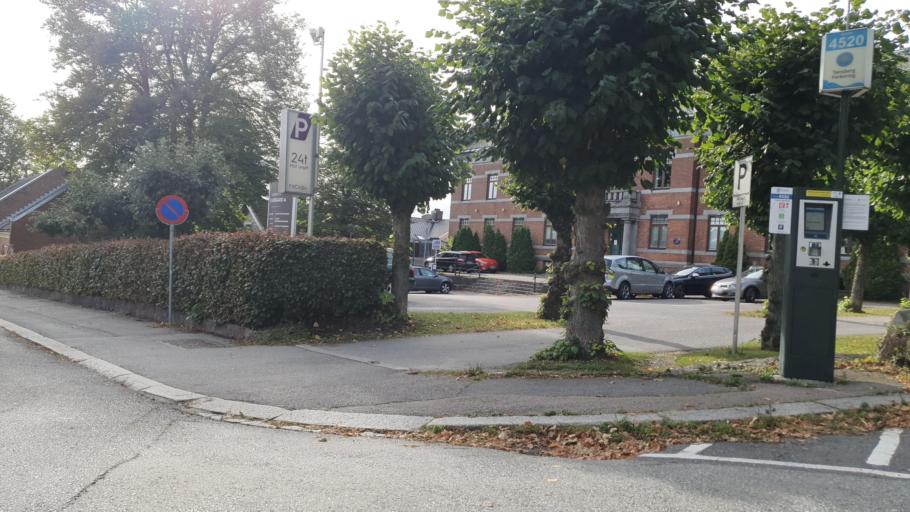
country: NO
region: Vestfold
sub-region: Tonsberg
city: Tonsberg
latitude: 59.2666
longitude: 10.4141
